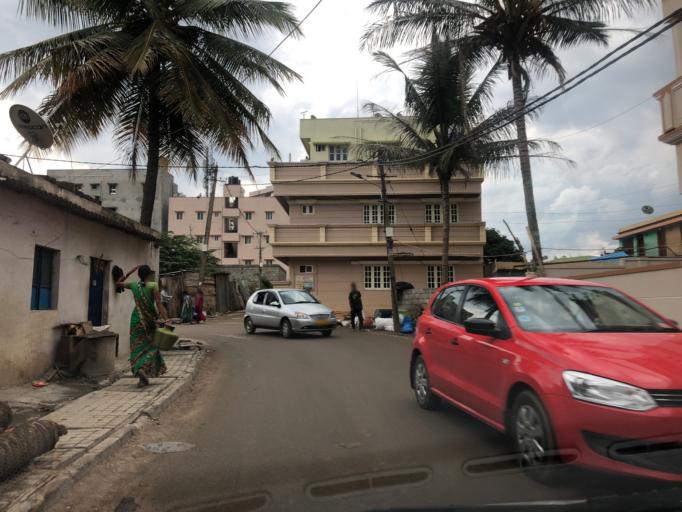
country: IN
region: Karnataka
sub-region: Bangalore Urban
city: Bangalore
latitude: 12.9900
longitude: 77.6981
